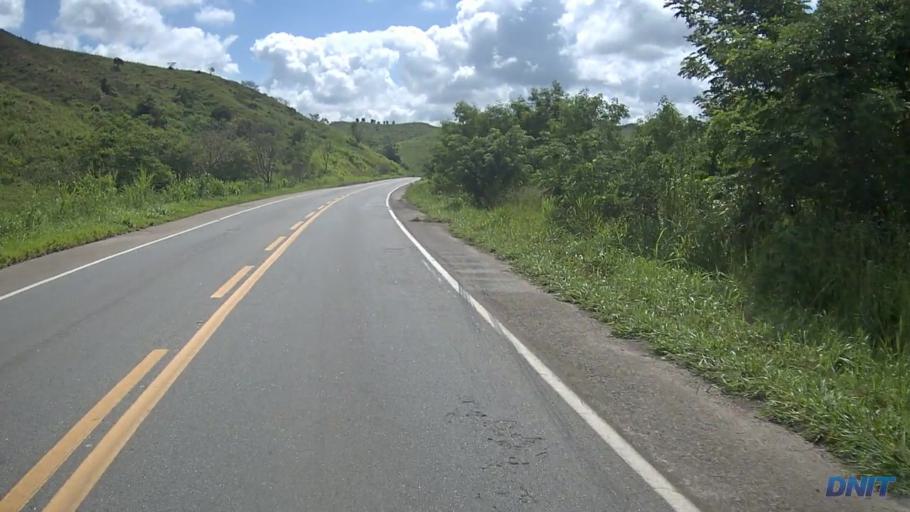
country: BR
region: Minas Gerais
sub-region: Belo Oriente
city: Belo Oriente
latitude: -19.1392
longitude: -42.2202
